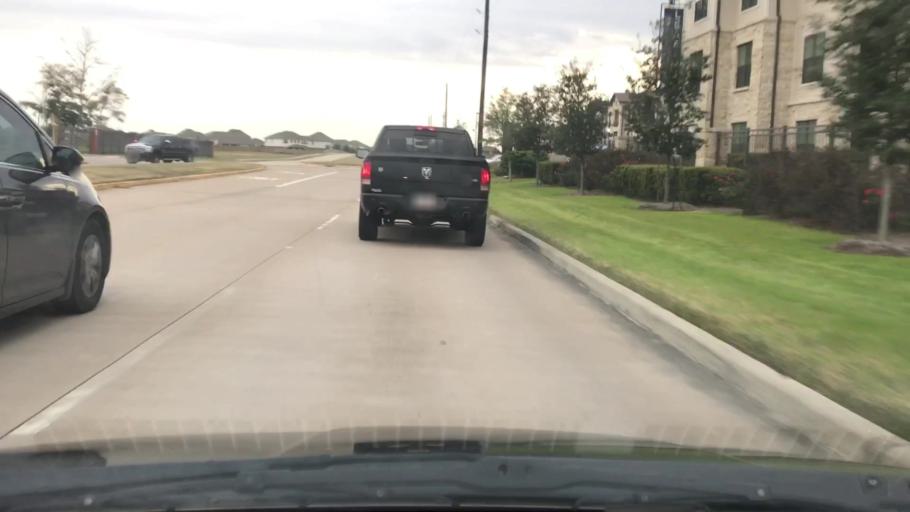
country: US
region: Texas
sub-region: Fort Bend County
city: Cinco Ranch
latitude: 29.7396
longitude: -95.7957
